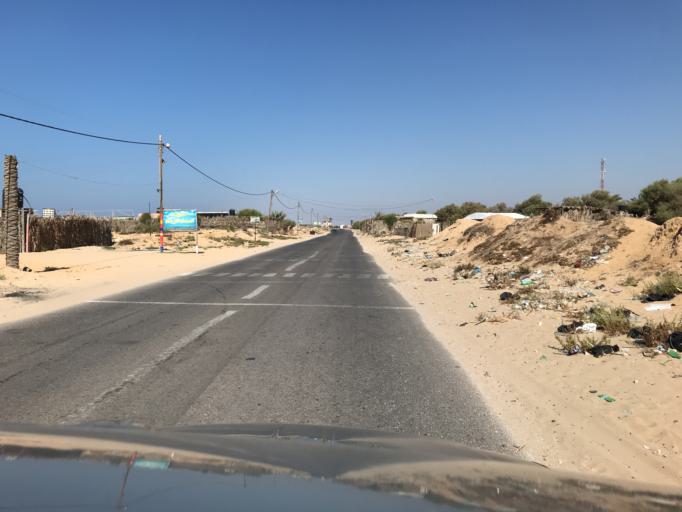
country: PS
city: Wadi as Salqa
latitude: 31.3939
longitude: 34.3012
